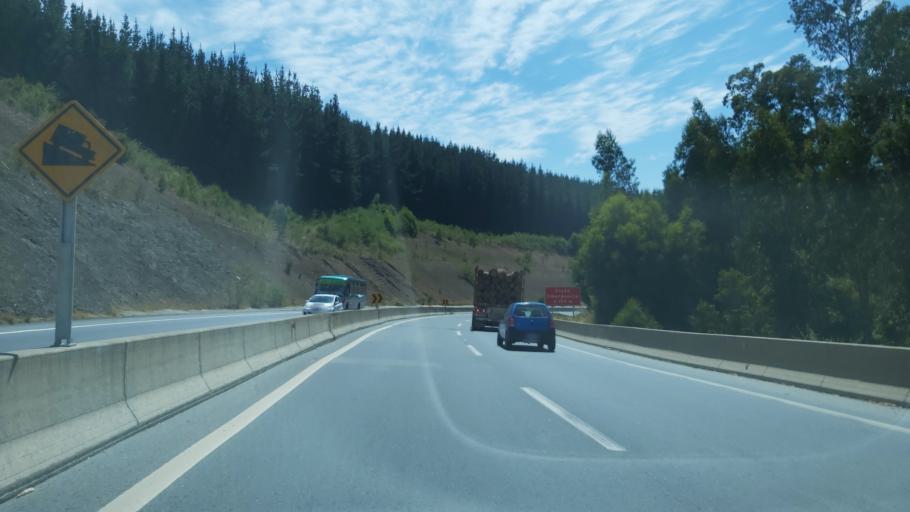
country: CL
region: Biobio
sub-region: Provincia de Concepcion
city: Lota
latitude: -37.1014
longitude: -73.1457
